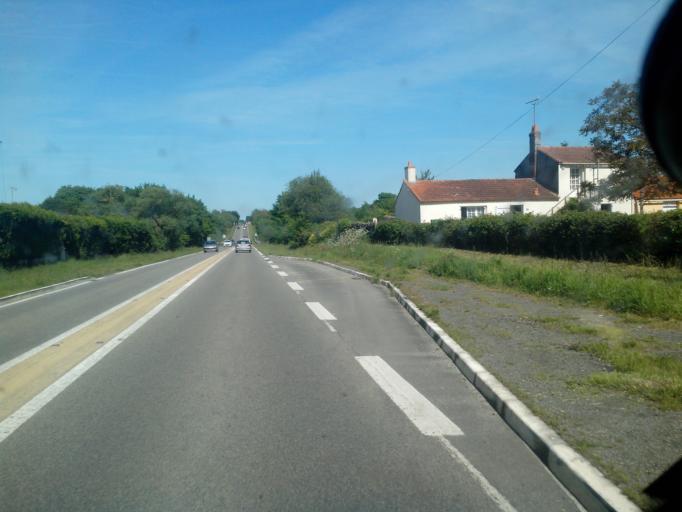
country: FR
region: Pays de la Loire
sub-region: Departement de la Loire-Atlantique
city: Arthon-en-Retz
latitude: 47.1117
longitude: -1.9712
